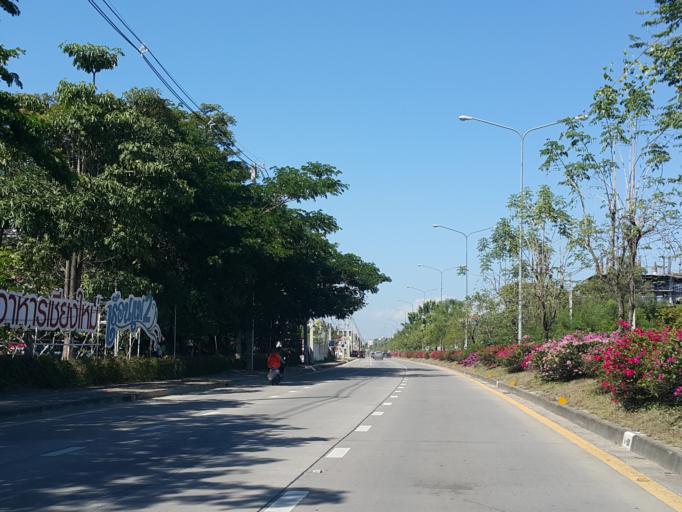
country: TH
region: Chiang Mai
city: San Sai
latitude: 18.8372
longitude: 99.0014
